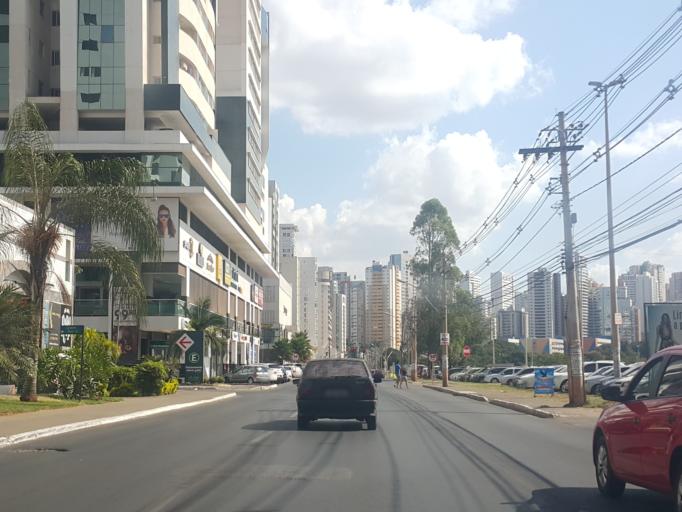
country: BR
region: Federal District
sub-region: Brasilia
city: Brasilia
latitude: -15.8360
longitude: -48.0193
